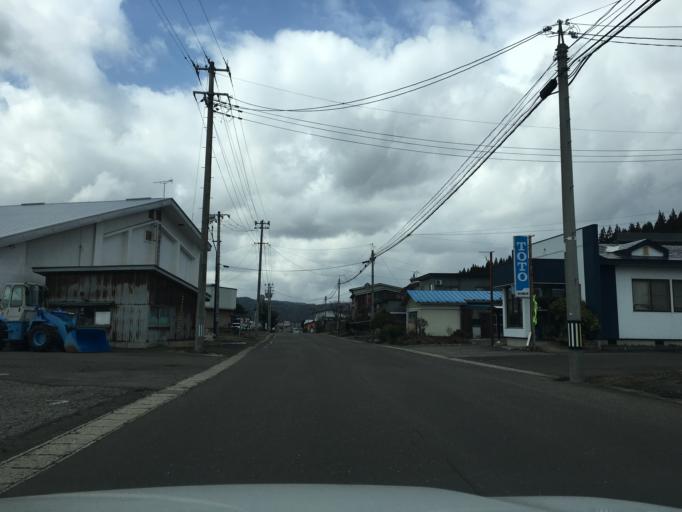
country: JP
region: Akita
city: Takanosu
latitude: 40.1626
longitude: 140.3265
